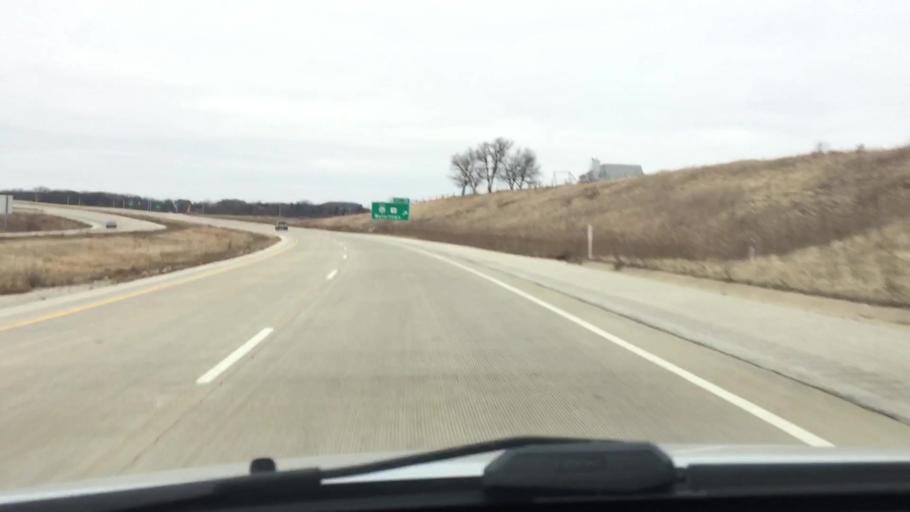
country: US
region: Wisconsin
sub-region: Jefferson County
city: Watertown
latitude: 43.1515
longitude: -88.7355
